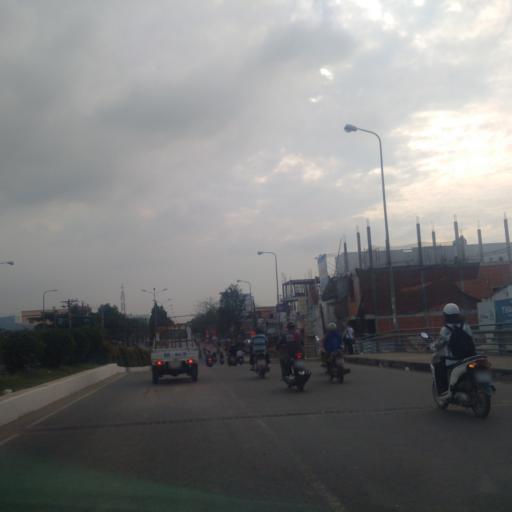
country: VN
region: Can Tho
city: Can Tho
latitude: 10.0425
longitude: 105.7642
